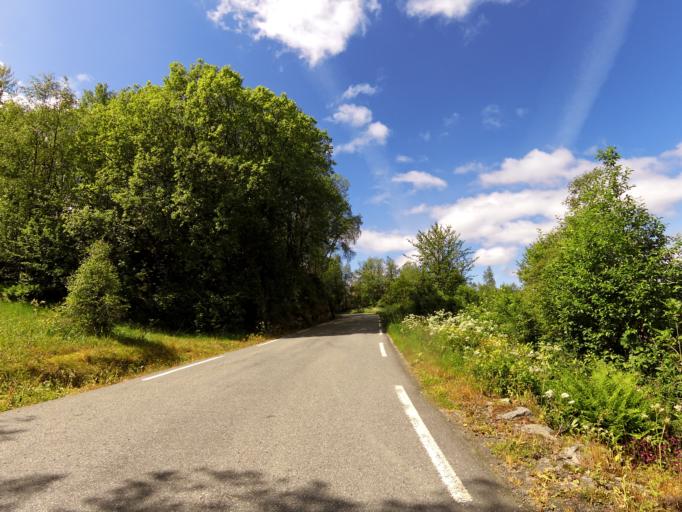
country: NO
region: Vest-Agder
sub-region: Kvinesdal
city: Liknes
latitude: 58.2873
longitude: 6.9389
